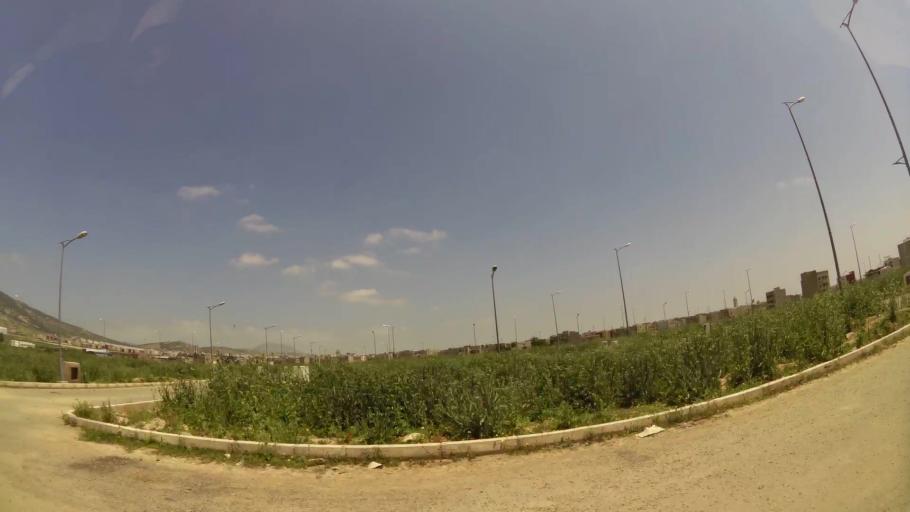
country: MA
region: Fes-Boulemane
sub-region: Fes
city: Fes
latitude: 34.0380
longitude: -5.0570
